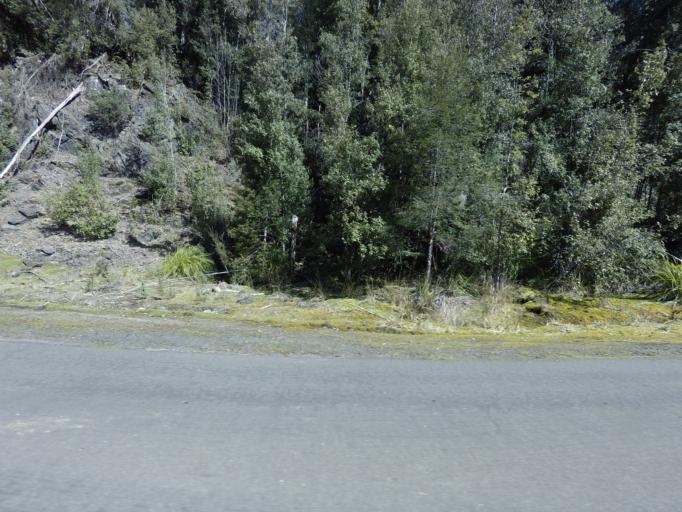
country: AU
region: Tasmania
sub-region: Derwent Valley
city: New Norfolk
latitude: -42.7458
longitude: 146.5009
